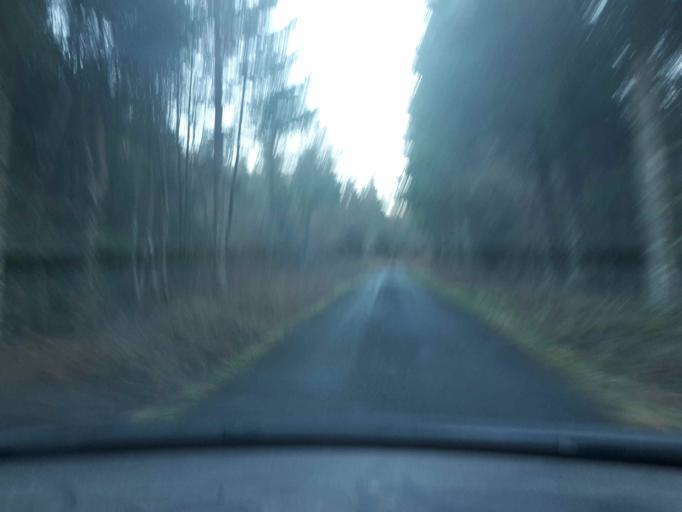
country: FR
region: Auvergne
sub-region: Departement du Cantal
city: Riom-es-Montagnes
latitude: 45.2135
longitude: 2.5787
